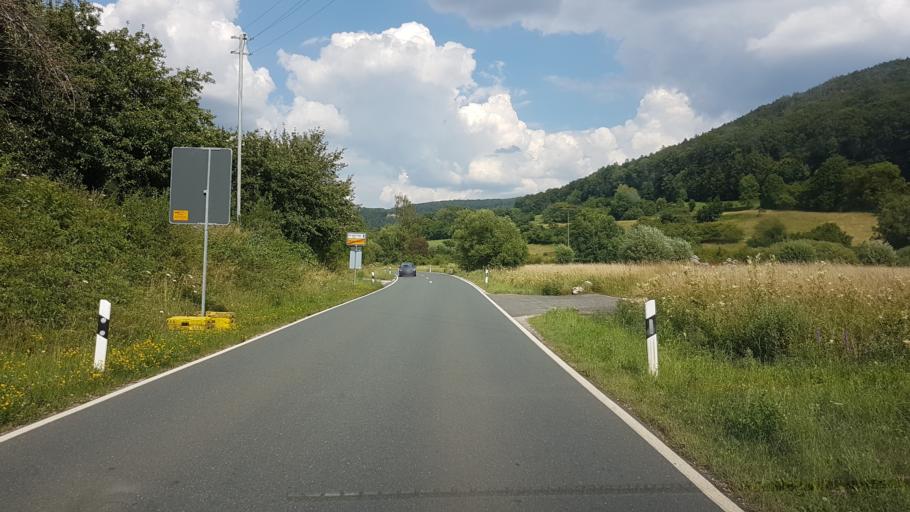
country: DE
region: Bavaria
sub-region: Upper Franconia
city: Pretzfeld
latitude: 49.7475
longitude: 11.2142
